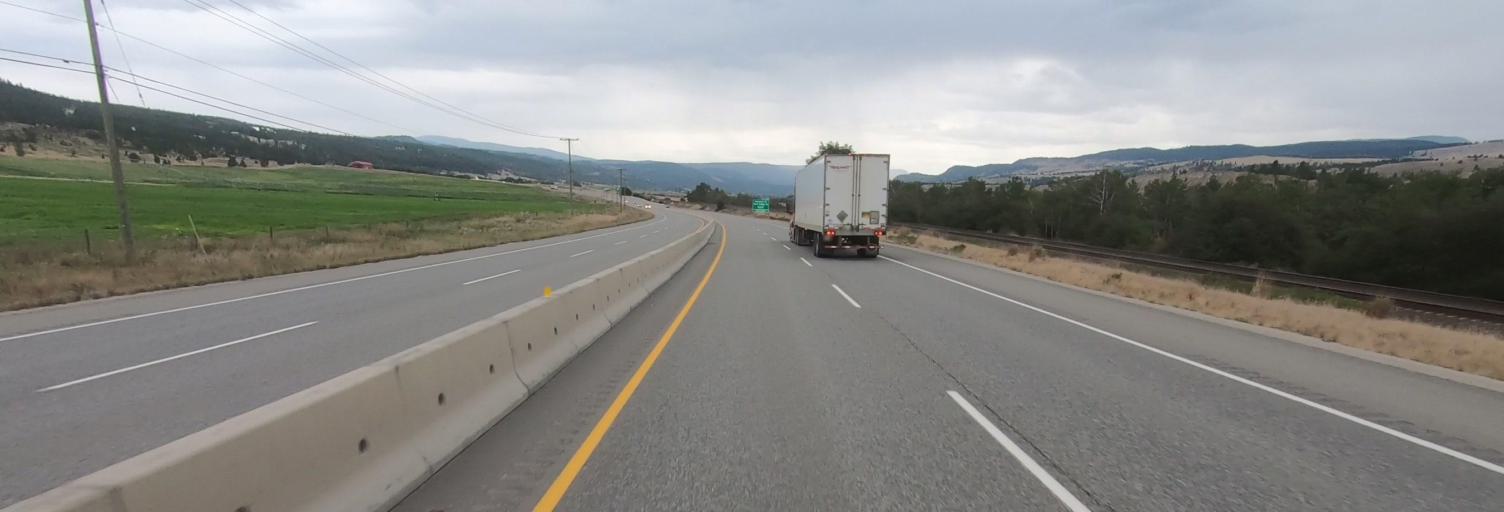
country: CA
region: British Columbia
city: Chase
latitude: 50.6962
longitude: -119.8061
